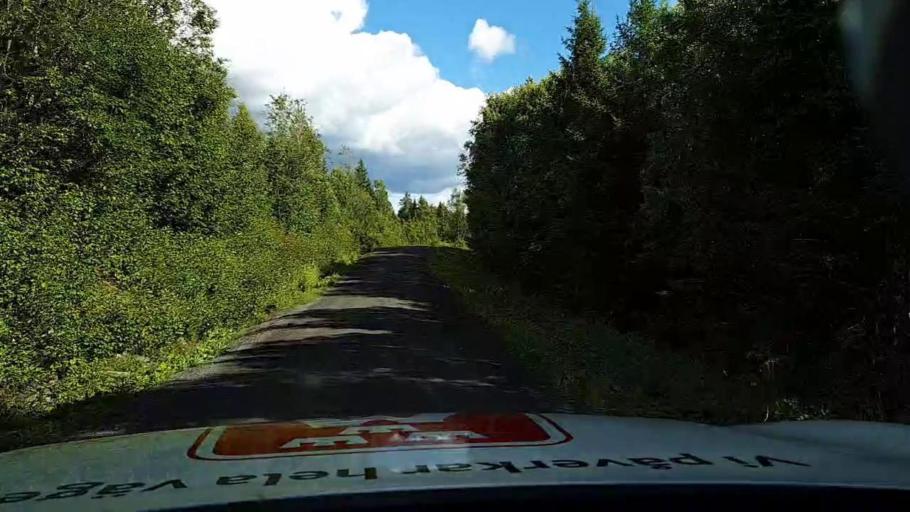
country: SE
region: Jaemtland
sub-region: Krokoms Kommun
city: Valla
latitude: 63.3213
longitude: 13.7576
